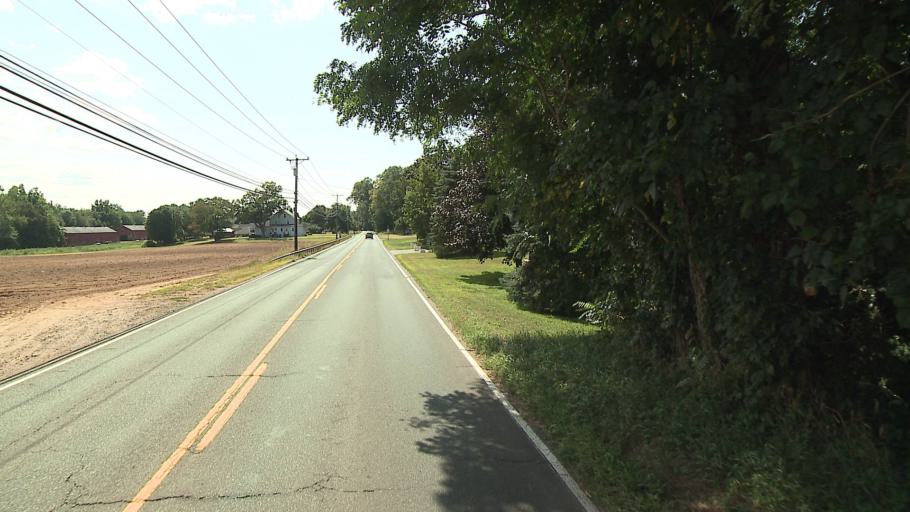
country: US
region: Connecticut
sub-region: Hartford County
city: Broad Brook
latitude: 41.9333
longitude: -72.5318
